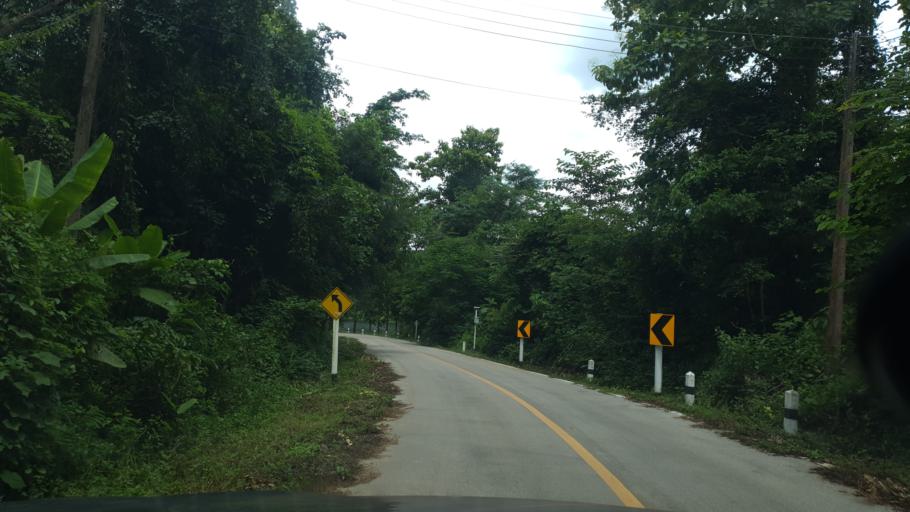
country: TH
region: Lampang
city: Hang Chat
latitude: 18.3620
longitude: 99.2602
